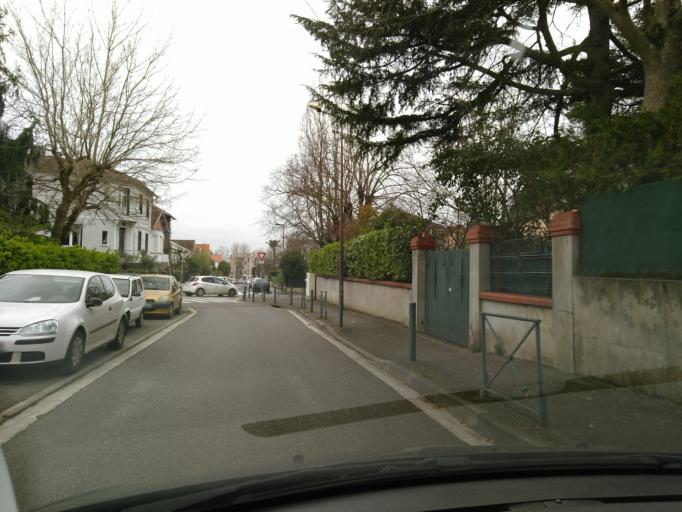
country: FR
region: Midi-Pyrenees
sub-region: Departement de la Haute-Garonne
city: Toulouse
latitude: 43.5943
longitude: 1.4701
